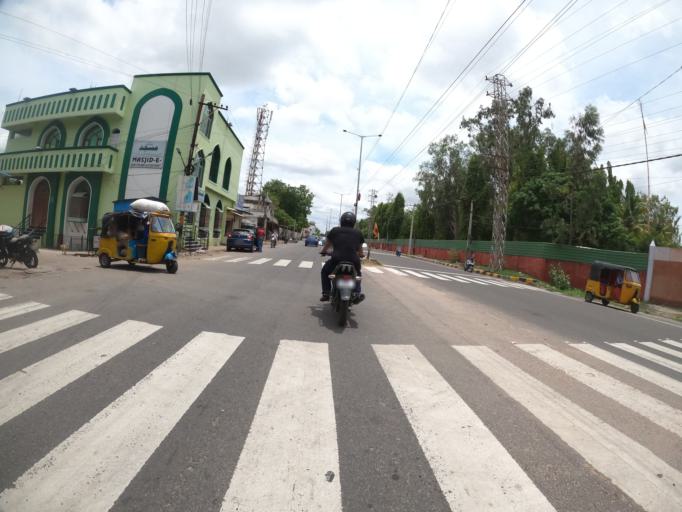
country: IN
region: Telangana
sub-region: Hyderabad
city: Hyderabad
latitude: 17.3754
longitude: 78.3955
